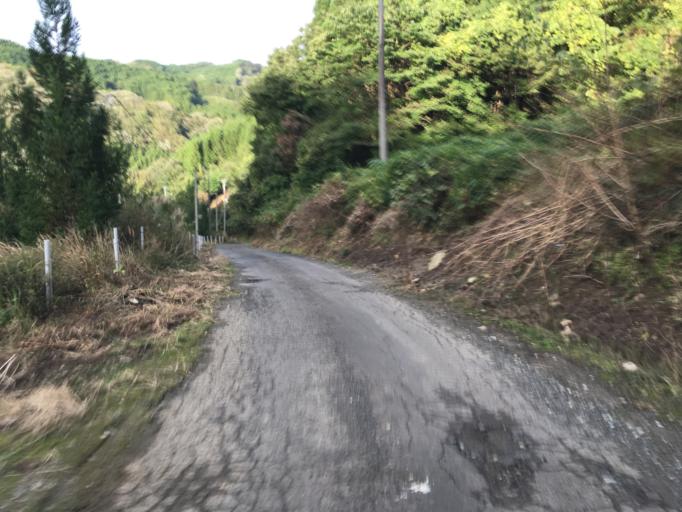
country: JP
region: Miyagi
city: Marumori
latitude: 37.9323
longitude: 140.7053
